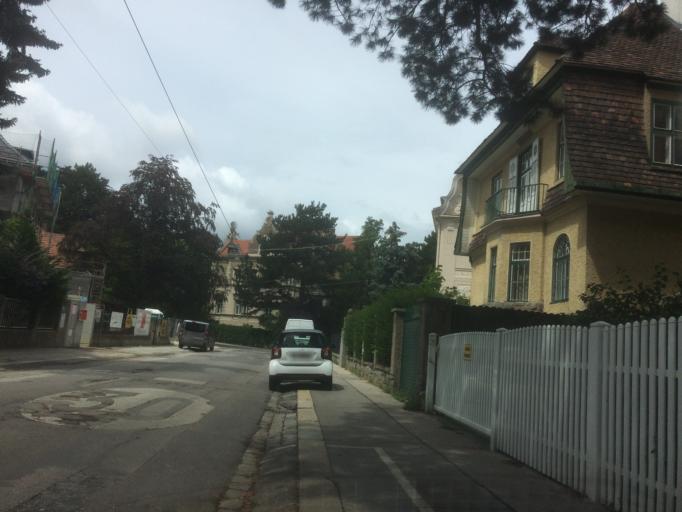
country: AT
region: Lower Austria
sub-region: Politischer Bezirk Modling
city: Perchtoldsdorf
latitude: 48.1852
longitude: 16.2951
